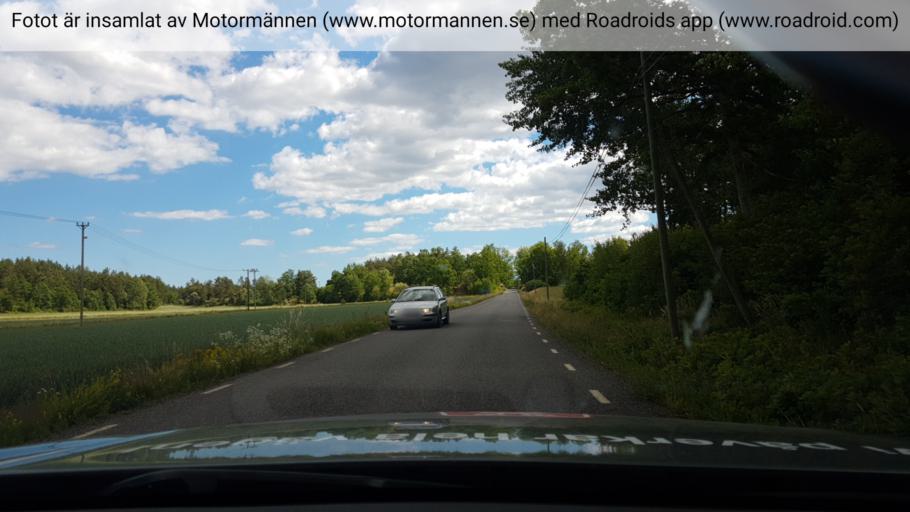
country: SE
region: Kalmar
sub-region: Vasterviks Kommun
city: Forserum
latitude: 57.9889
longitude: 16.6052
